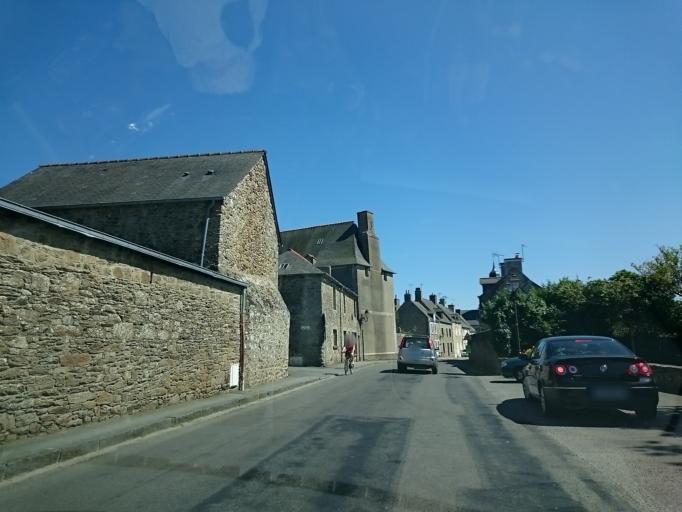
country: FR
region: Brittany
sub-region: Departement d'Ille-et-Vilaine
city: Saint-Coulomb
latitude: 48.6765
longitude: -1.9118
